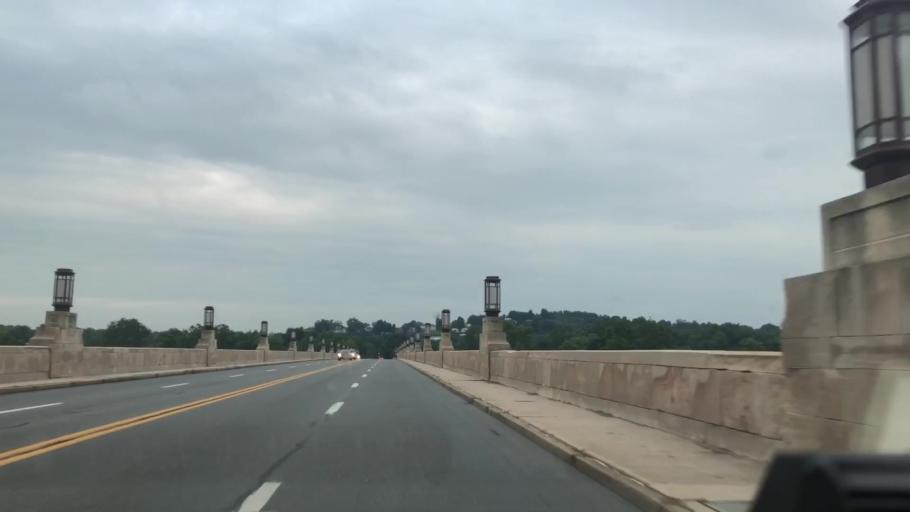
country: US
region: Pennsylvania
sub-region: Dauphin County
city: Harrisburg
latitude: 40.2579
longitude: -76.8835
